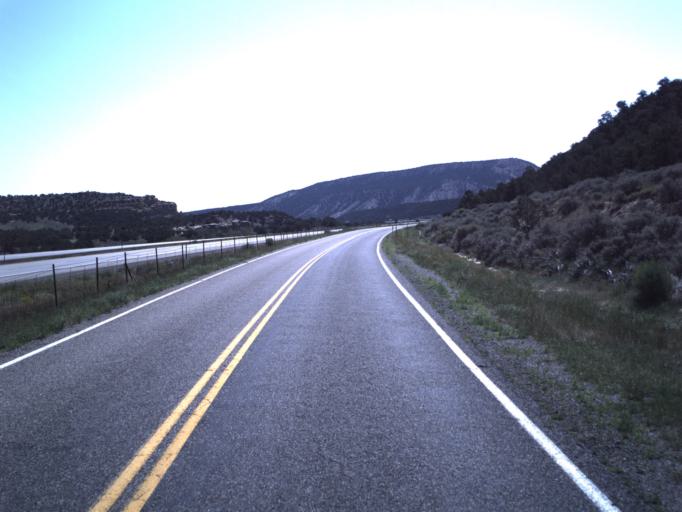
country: US
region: Utah
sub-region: Wayne County
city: Loa
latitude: 38.7575
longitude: -111.4081
